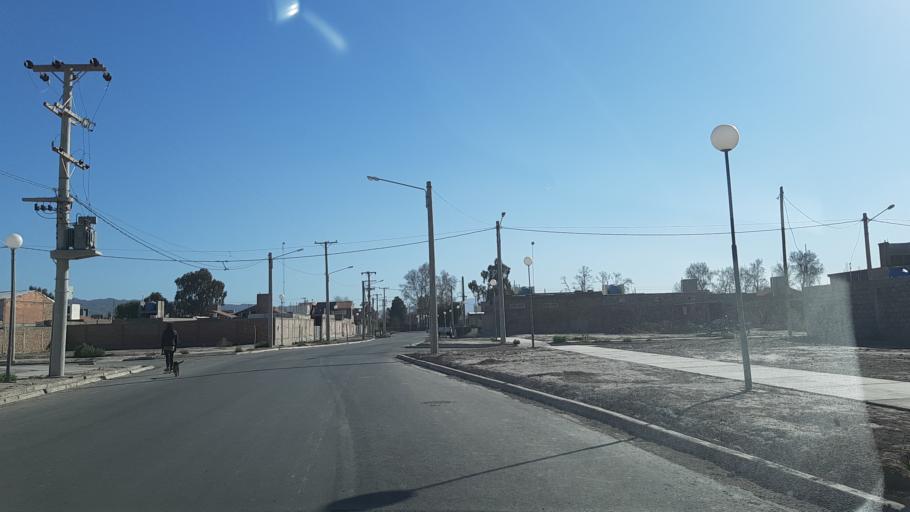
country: AR
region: San Juan
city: San Juan
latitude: -31.5179
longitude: -68.5911
